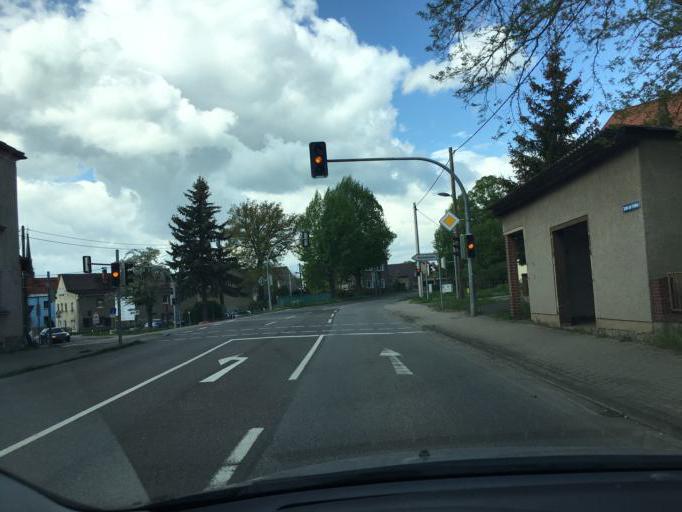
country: DE
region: Saxony
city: Frohburg
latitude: 51.0830
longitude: 12.5326
